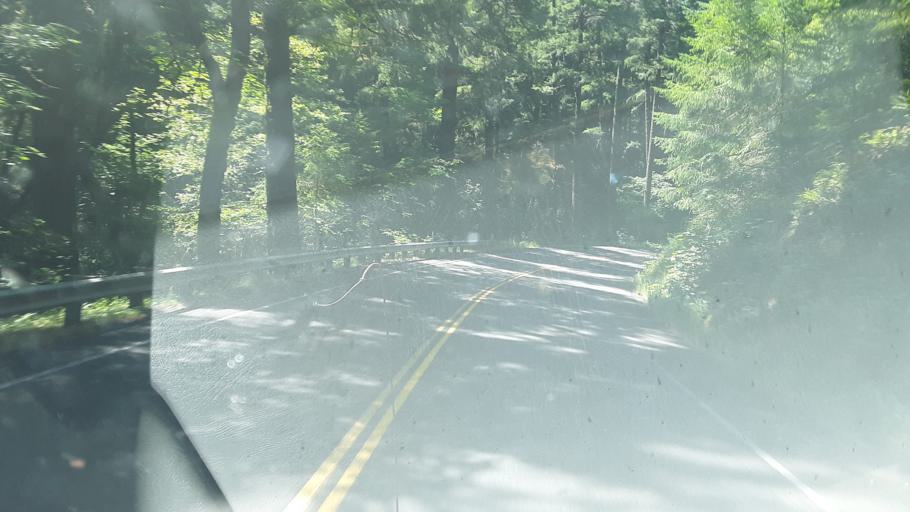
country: US
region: Oregon
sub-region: Josephine County
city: Cave Junction
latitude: 41.9309
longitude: -123.7566
